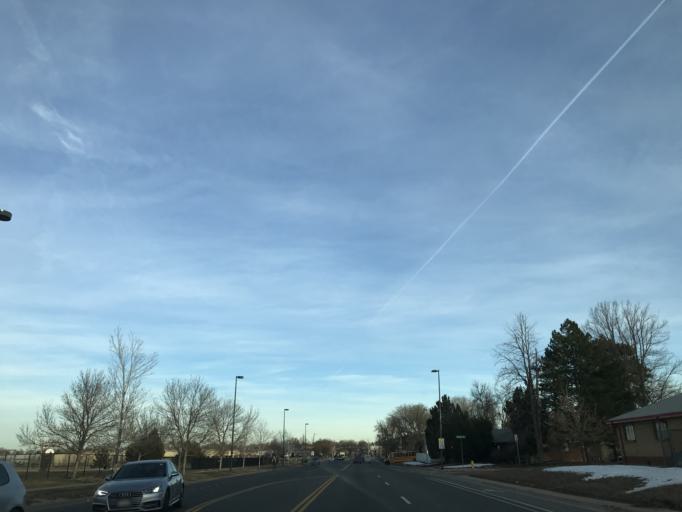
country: US
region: Colorado
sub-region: Adams County
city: Aurora
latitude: 39.7474
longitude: -104.8830
